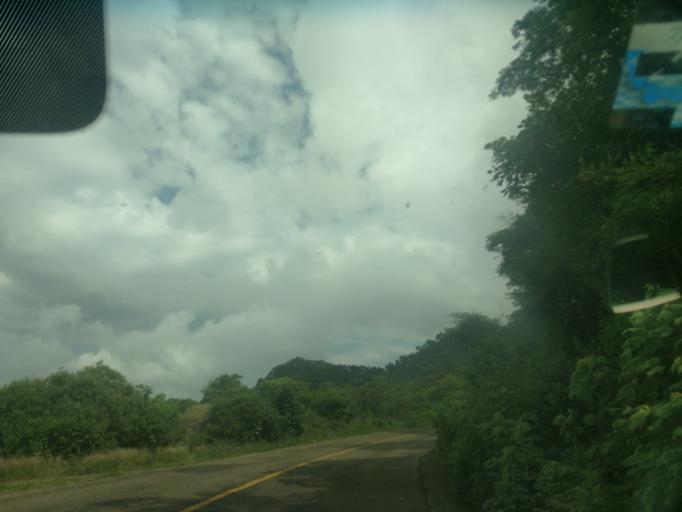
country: MX
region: Jalisco
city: El Salto
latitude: 20.3634
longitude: -104.5893
